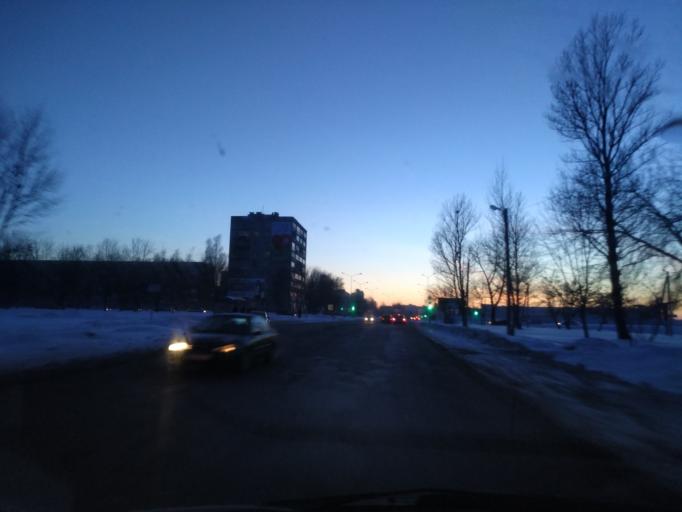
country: BY
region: Mogilev
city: Mahilyow
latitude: 53.8816
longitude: 30.3228
